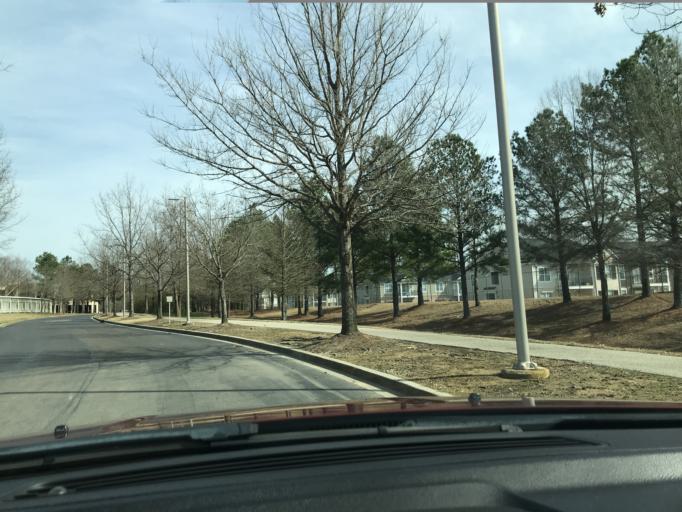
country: US
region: Tennessee
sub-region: Shelby County
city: Collierville
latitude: 35.0322
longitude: -89.7230
